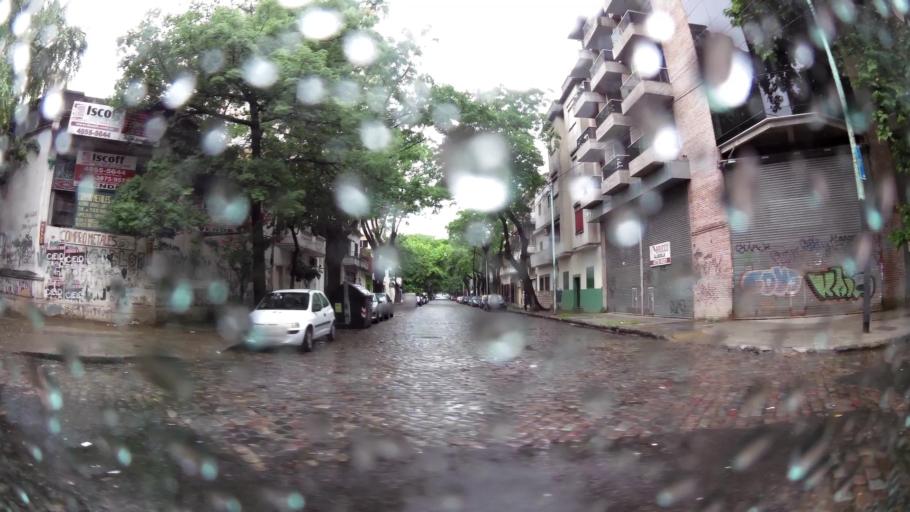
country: AR
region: Buenos Aires F.D.
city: Colegiales
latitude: -34.5945
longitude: -58.4351
